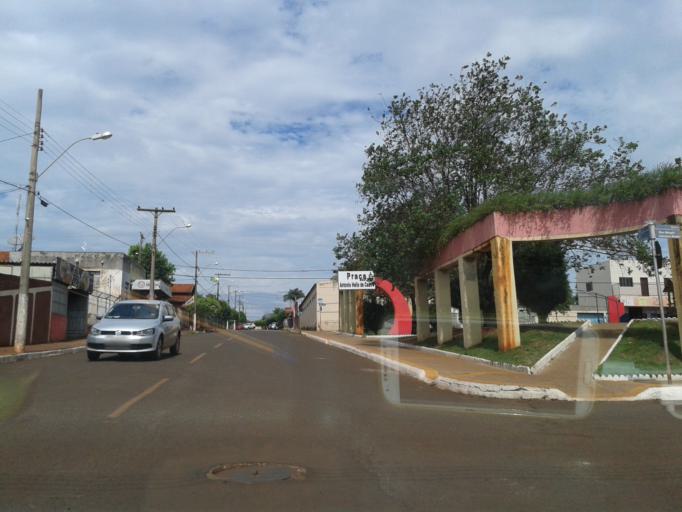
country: BR
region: Goias
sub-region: Itumbiara
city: Itumbiara
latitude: -18.4366
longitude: -49.1859
